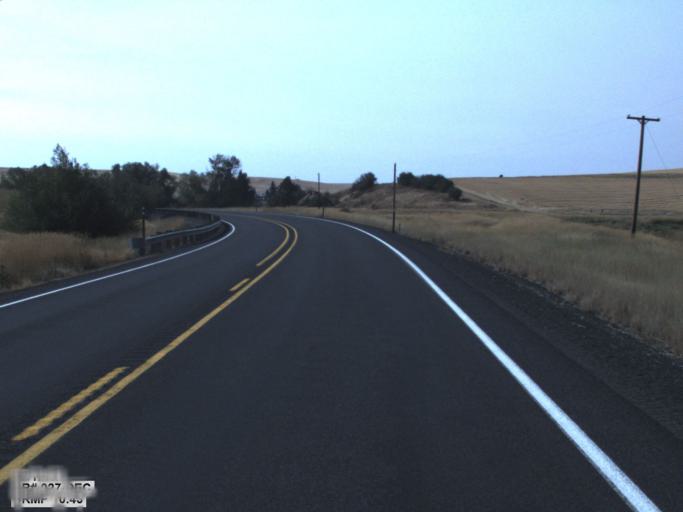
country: US
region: Washington
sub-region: Whitman County
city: Pullman
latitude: 46.8618
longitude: -117.1307
